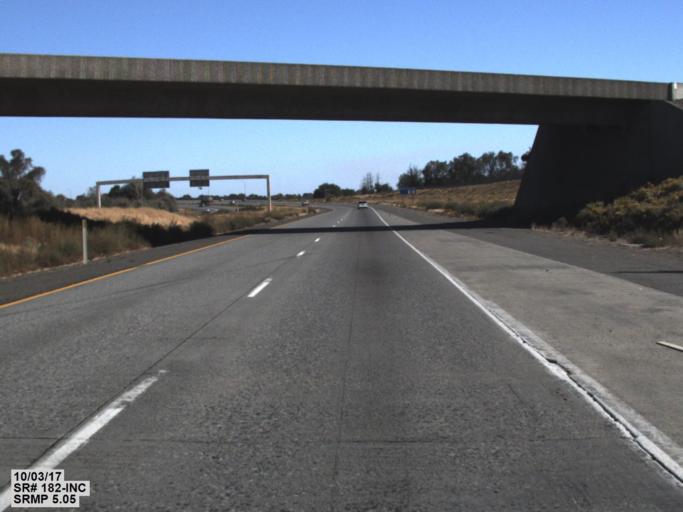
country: US
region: Washington
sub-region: Benton County
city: Richland
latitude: 46.2586
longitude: -119.2608
